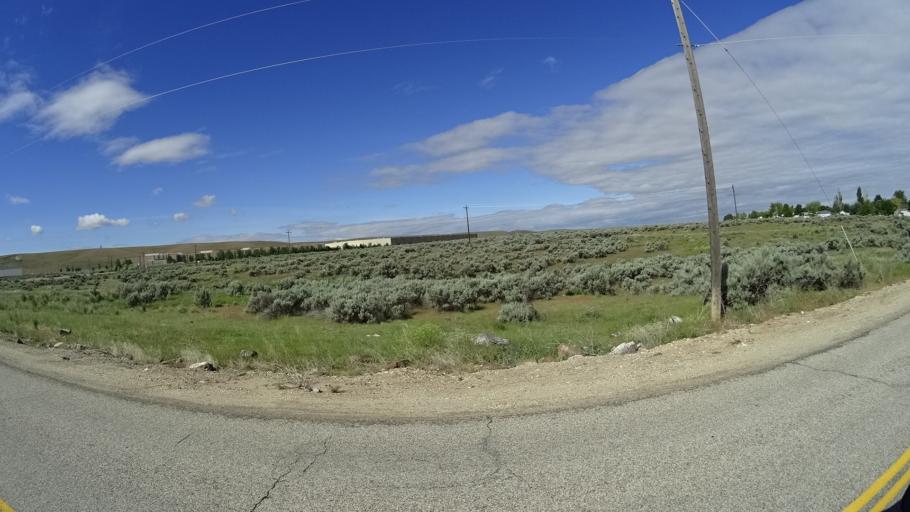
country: US
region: Idaho
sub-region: Ada County
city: Boise
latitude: 43.5230
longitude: -116.1521
